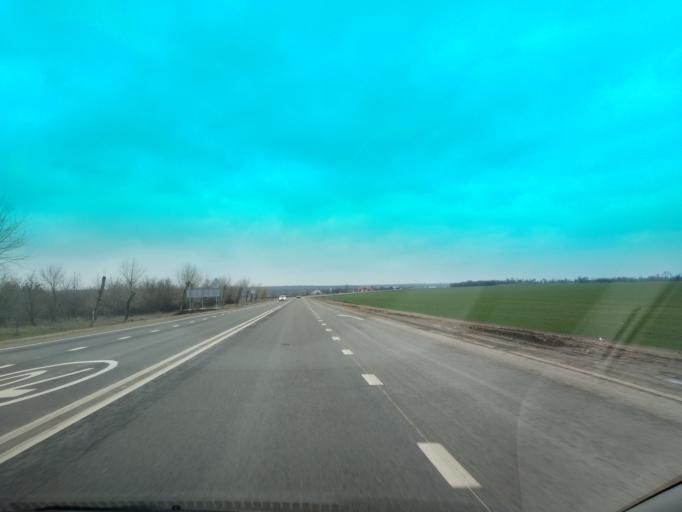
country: RU
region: Krasnodarskiy
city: Novomalorossiyskaya
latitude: 45.7065
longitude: 39.8450
